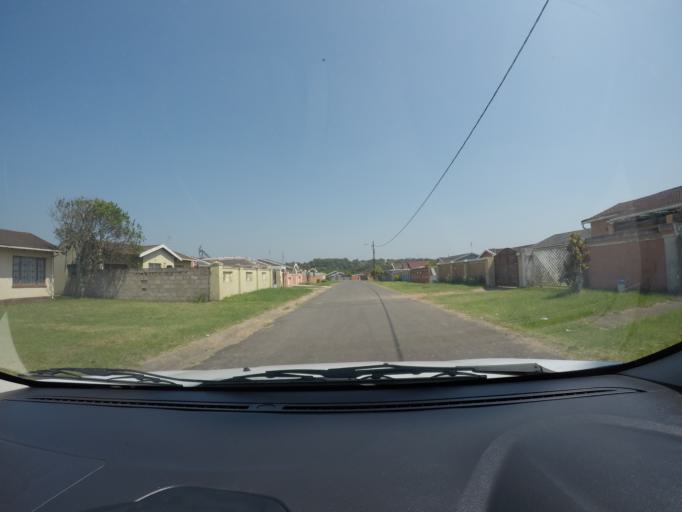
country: ZA
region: KwaZulu-Natal
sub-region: uThungulu District Municipality
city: eSikhawini
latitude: -28.8614
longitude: 31.9193
